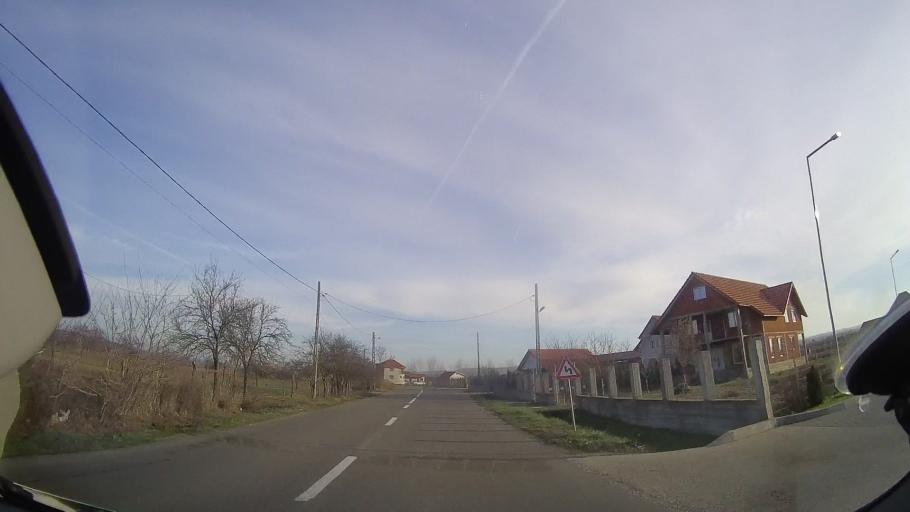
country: RO
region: Bihor
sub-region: Comuna Tileagd
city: Tileagd
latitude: 47.0667
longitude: 22.2118
